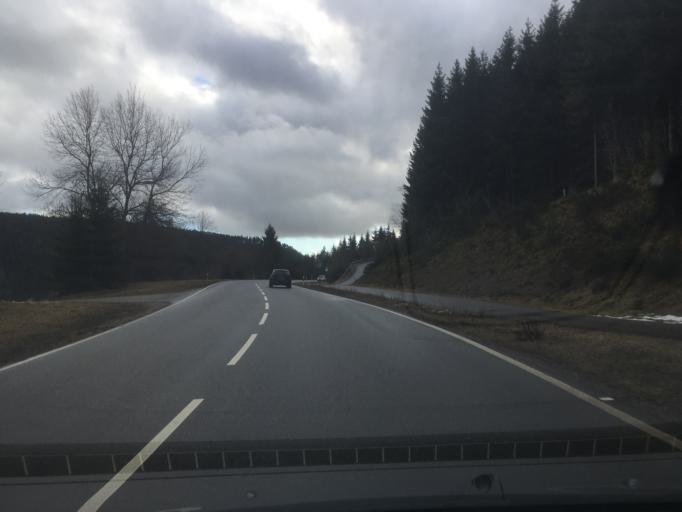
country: DE
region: Baden-Wuerttemberg
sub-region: Freiburg Region
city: Hausern
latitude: 47.7661
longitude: 8.1829
